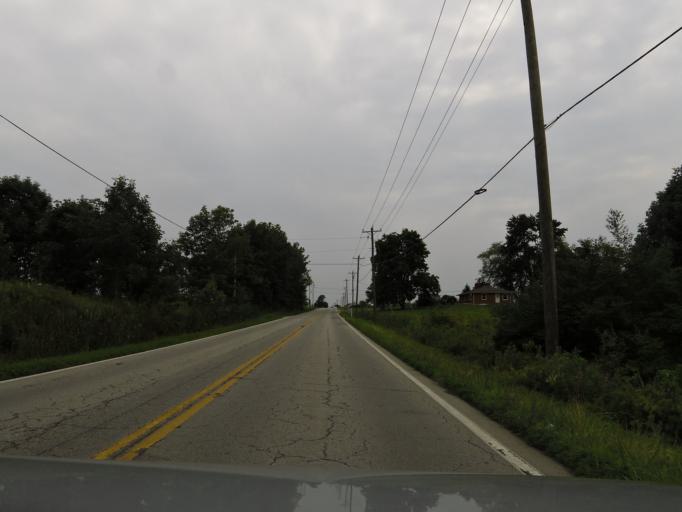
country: US
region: Ohio
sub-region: Clinton County
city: Blanchester
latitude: 39.2689
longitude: -83.9024
